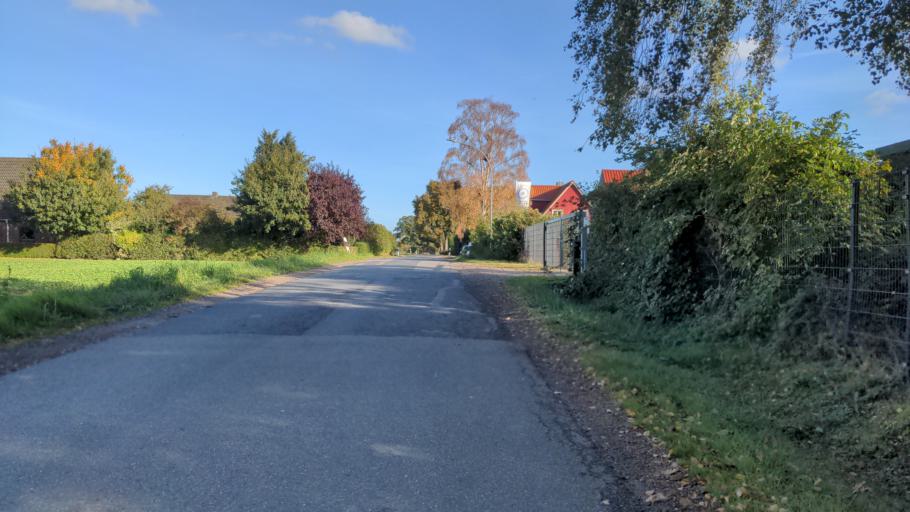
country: DE
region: Schleswig-Holstein
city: Manhagen
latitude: 54.1979
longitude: 10.8906
